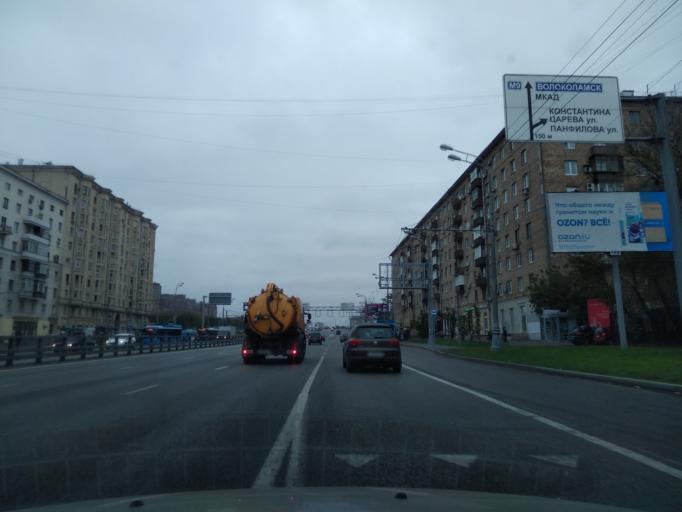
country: RU
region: Moskovskaya
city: Koptevo
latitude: 55.8091
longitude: 37.4954
